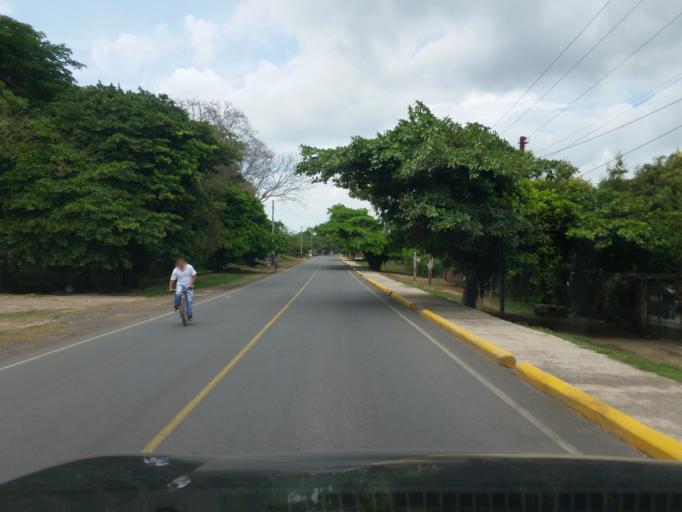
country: NI
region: Granada
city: Diria
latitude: 11.8809
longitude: -86.0534
